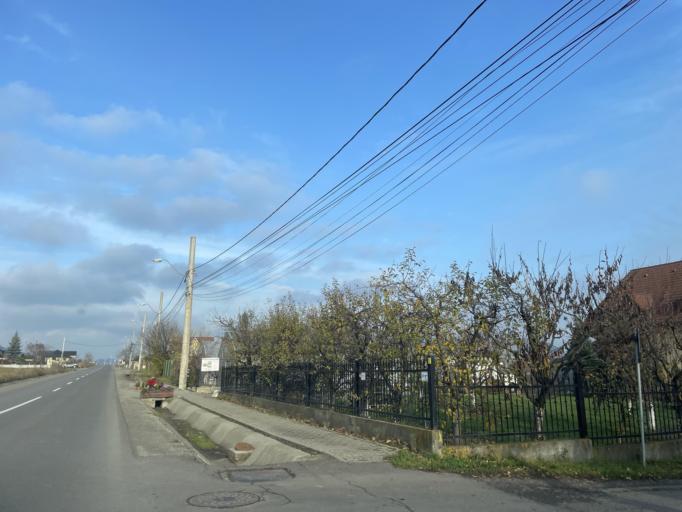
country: RO
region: Mures
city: Reghin-Sat
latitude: 46.7931
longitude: 24.7045
